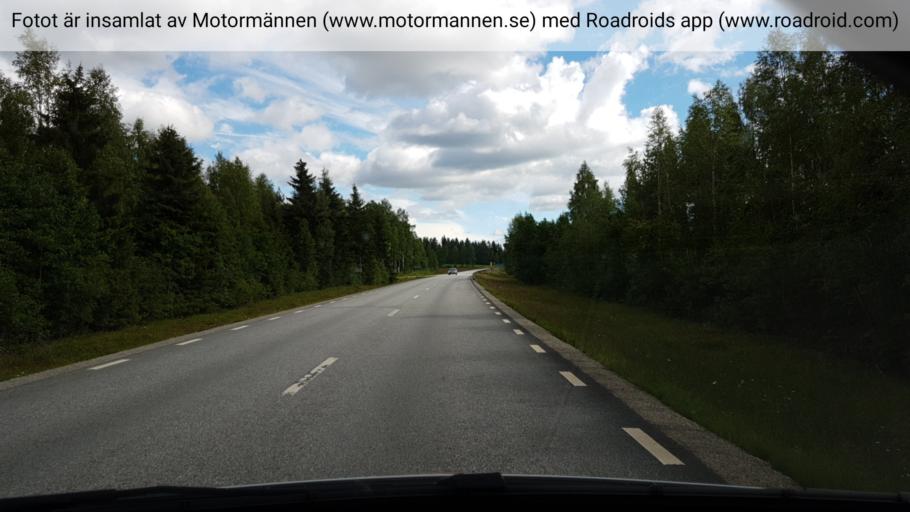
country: SE
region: Vaesterbotten
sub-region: Vindelns Kommun
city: Vindeln
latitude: 64.1842
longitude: 19.4723
